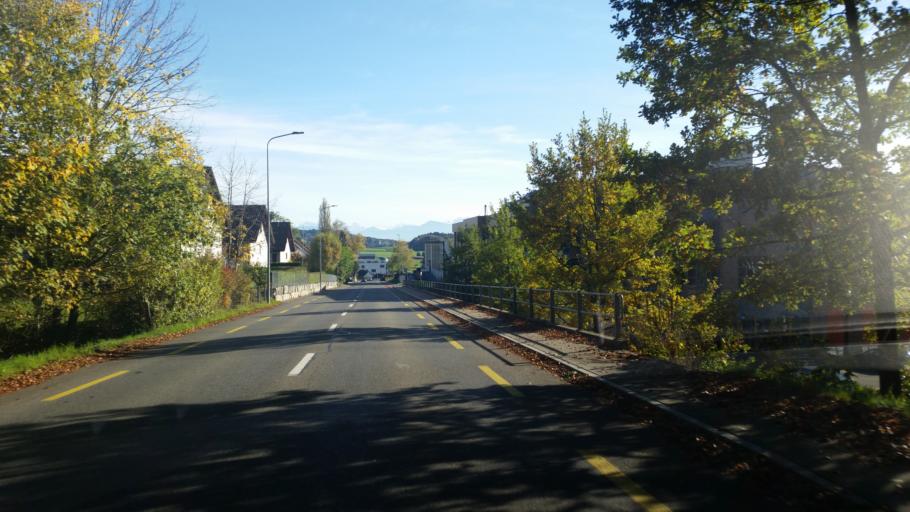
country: CH
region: Aargau
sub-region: Bezirk Baden
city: Niederrohrdorf
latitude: 47.4120
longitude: 8.3137
